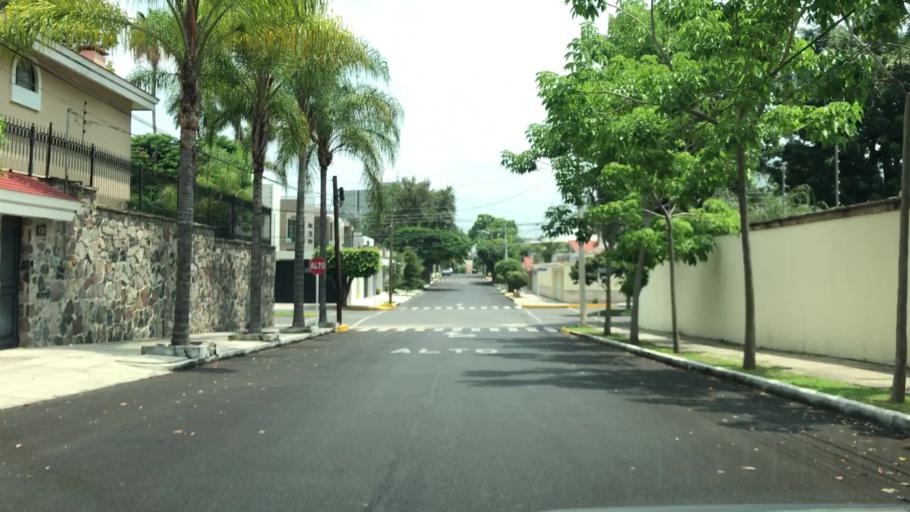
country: MX
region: Jalisco
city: Guadalajara
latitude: 20.6551
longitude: -103.4049
